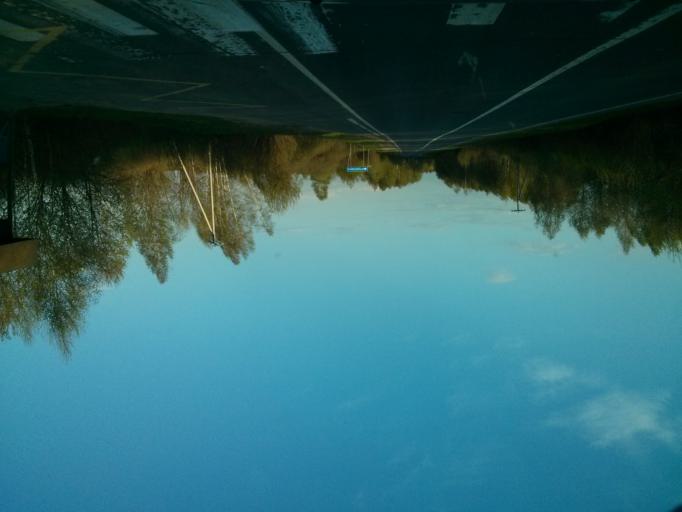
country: RU
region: Nizjnij Novgorod
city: Navashino
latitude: 55.7024
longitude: 42.3248
